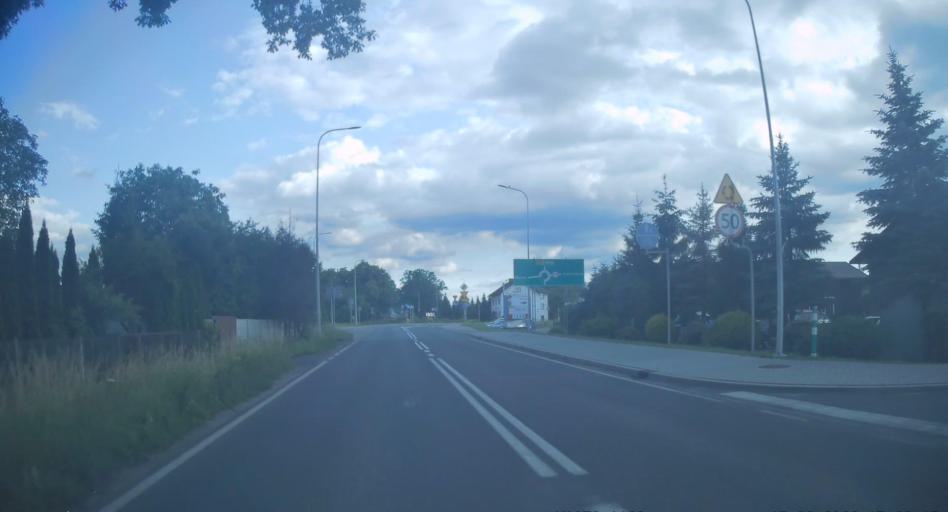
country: PL
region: Lesser Poland Voivodeship
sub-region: Powiat oswiecimski
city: Nowa Wies
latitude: 49.9398
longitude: 19.2109
